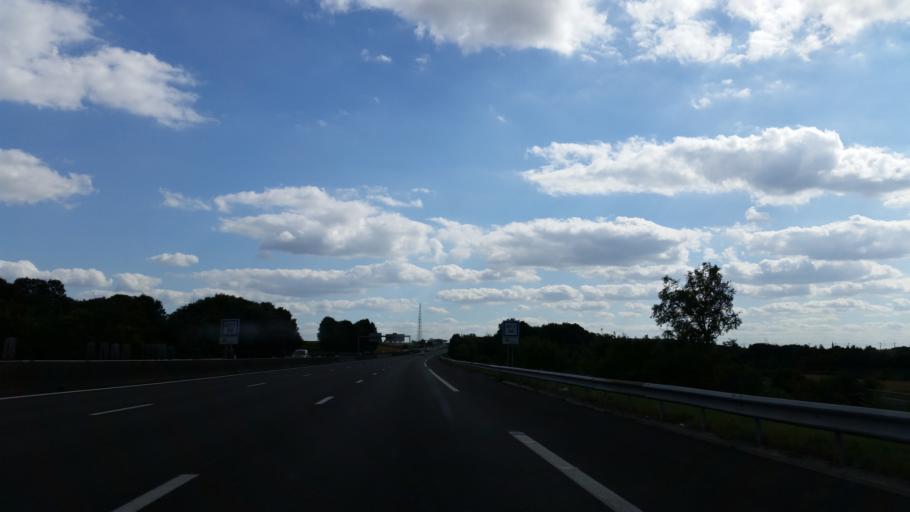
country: FR
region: Picardie
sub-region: Departement de la Somme
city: Moislains
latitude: 50.0208
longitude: 2.8831
